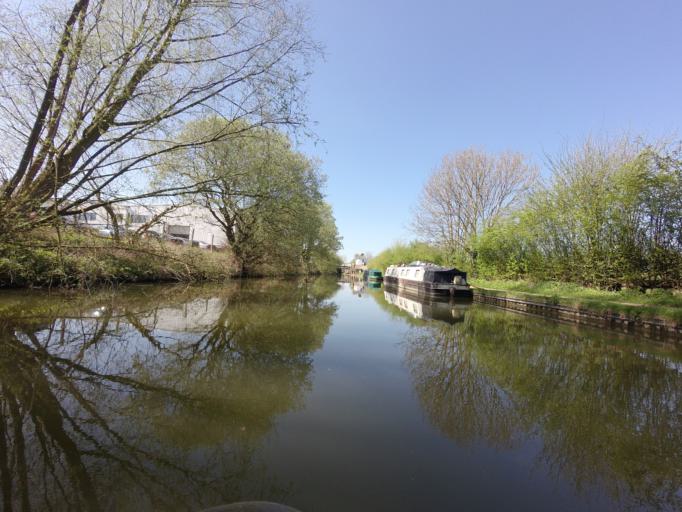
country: GB
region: England
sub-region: Hertfordshire
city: Tring
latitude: 51.7826
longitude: -0.6106
